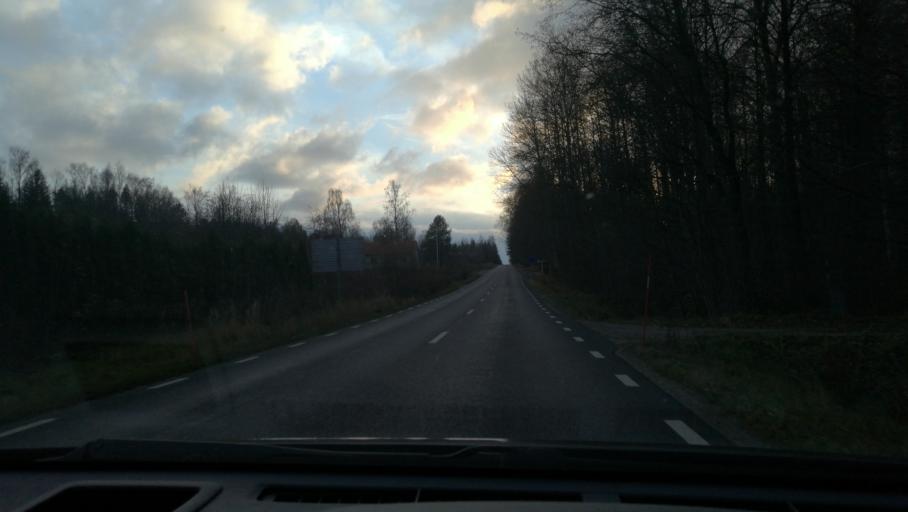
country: SE
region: Soedermanland
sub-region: Vingakers Kommun
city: Vingaker
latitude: 59.1616
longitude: 15.9362
